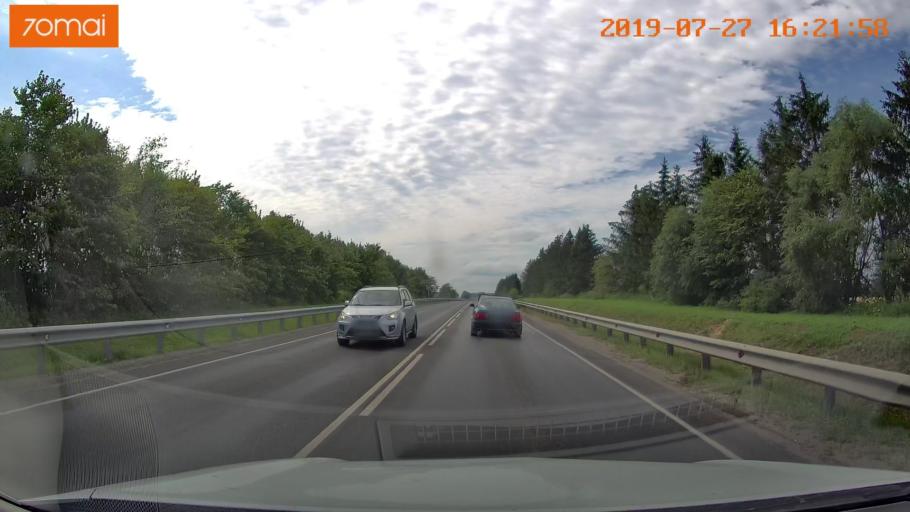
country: RU
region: Kaliningrad
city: Chernyakhovsk
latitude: 54.6263
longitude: 21.5044
